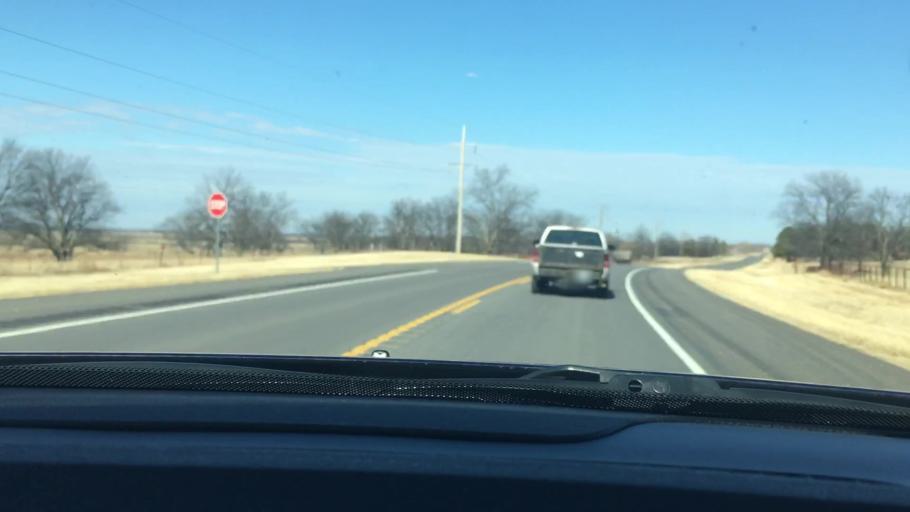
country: US
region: Oklahoma
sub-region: Garvin County
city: Wynnewood
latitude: 34.5797
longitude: -97.1424
